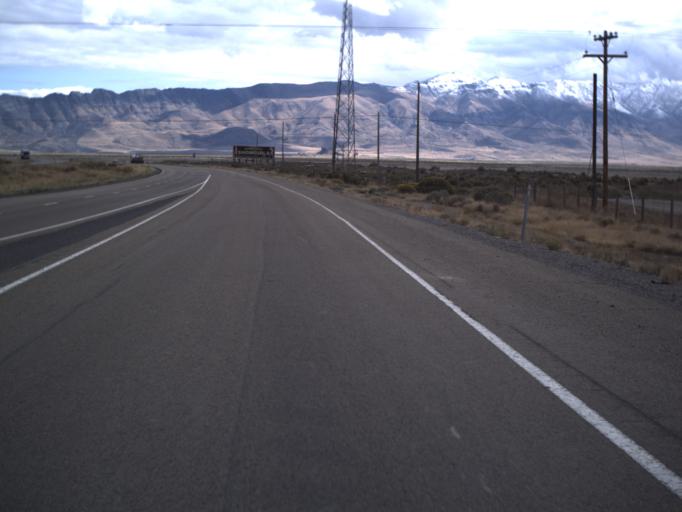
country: US
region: Utah
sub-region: Tooele County
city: Grantsville
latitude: 40.7604
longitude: -112.7775
